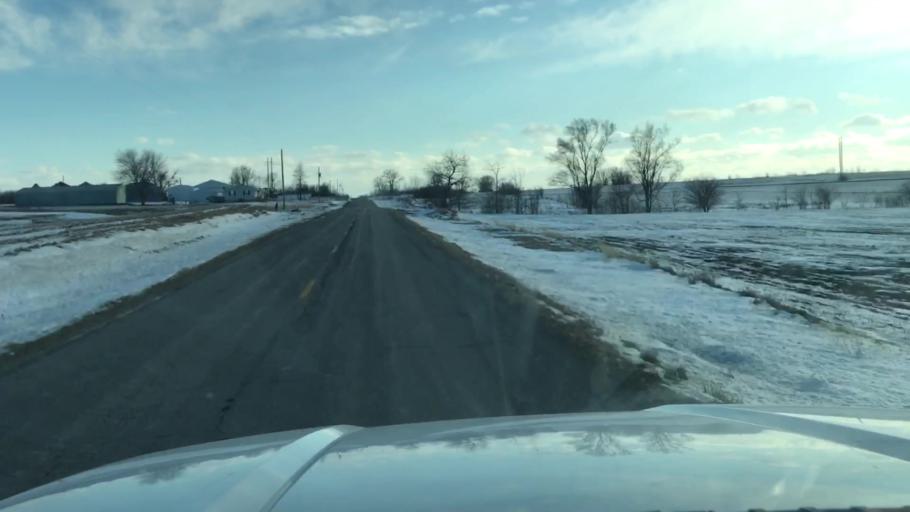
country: US
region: Missouri
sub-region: Holt County
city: Oregon
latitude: 40.1164
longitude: -95.0226
